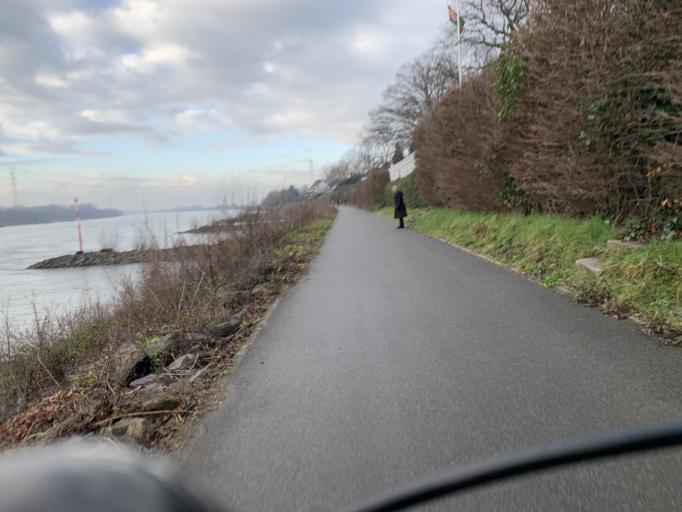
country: DE
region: North Rhine-Westphalia
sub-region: Regierungsbezirk Dusseldorf
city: Meerbusch
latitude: 51.3290
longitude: 6.7272
